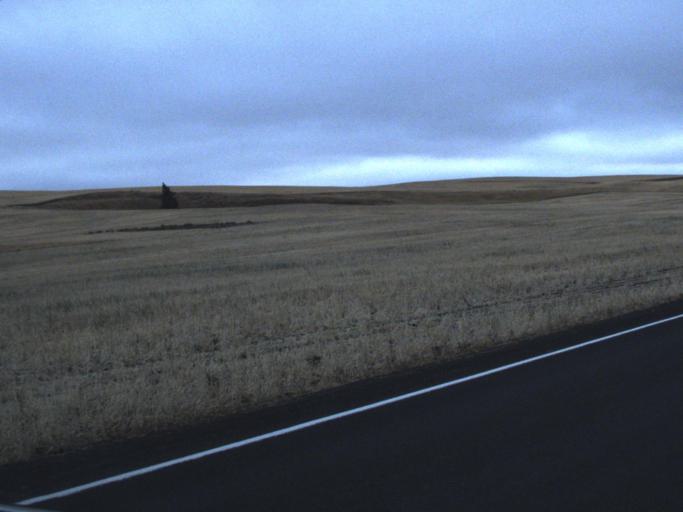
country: US
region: Washington
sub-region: Spokane County
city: Medical Lake
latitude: 47.7005
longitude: -117.8783
